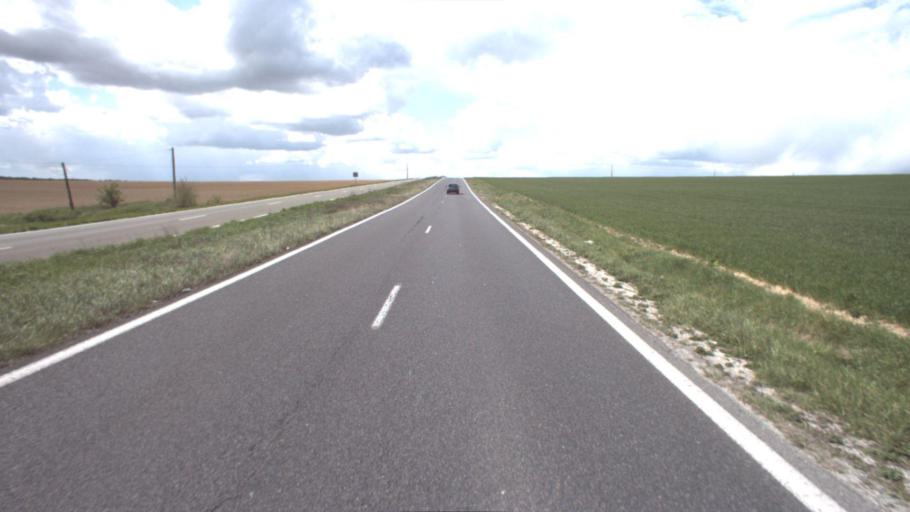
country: FR
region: Ile-de-France
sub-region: Departement de Seine-et-Marne
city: Touquin
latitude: 48.6851
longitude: 3.0543
